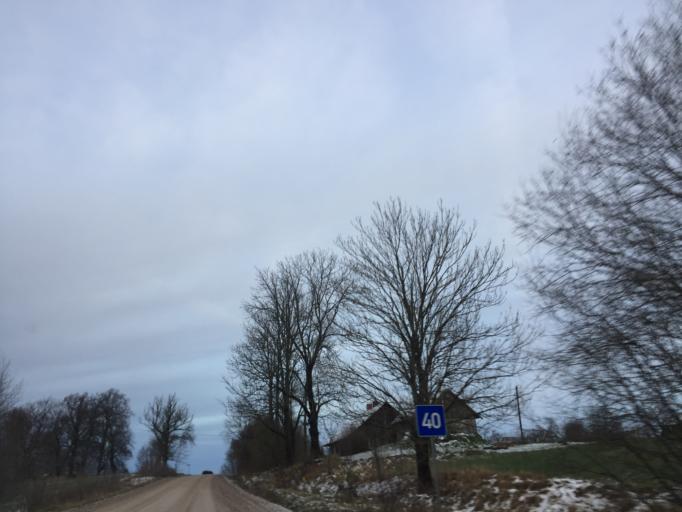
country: LV
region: Limbazu Rajons
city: Limbazi
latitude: 57.5847
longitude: 24.8358
